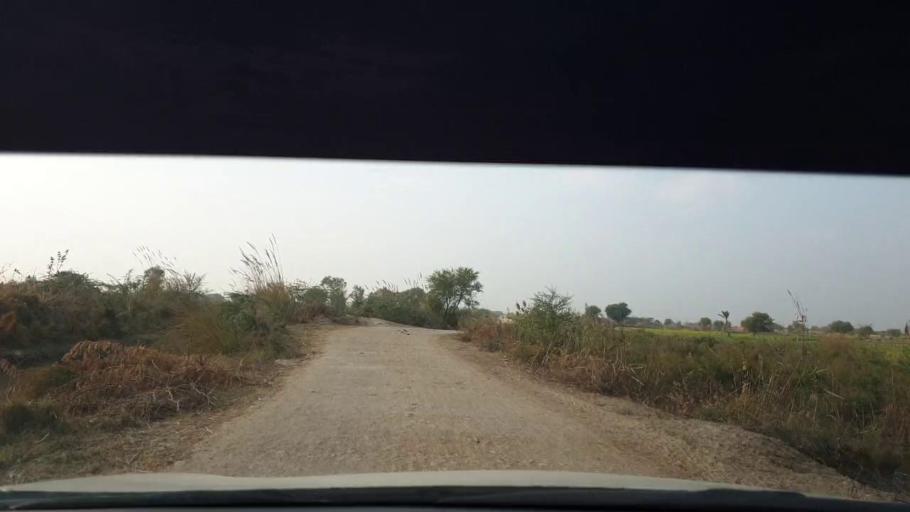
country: PK
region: Sindh
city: Berani
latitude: 25.7415
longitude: 68.9540
